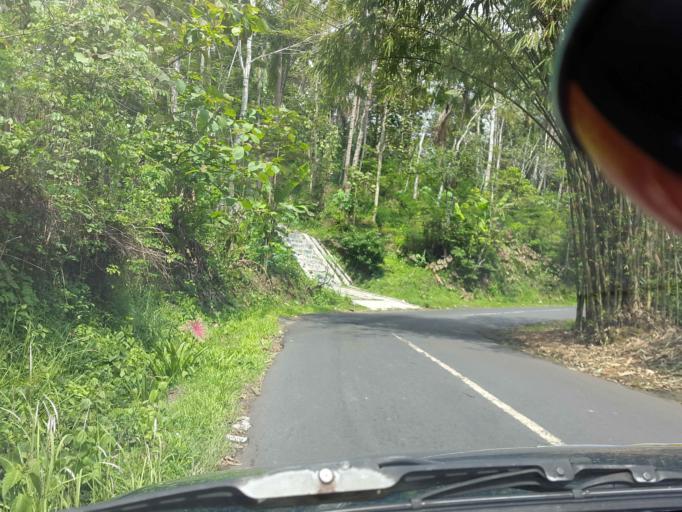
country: ID
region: Central Java
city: Mertoyudan
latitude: -7.5600
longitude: 110.0863
